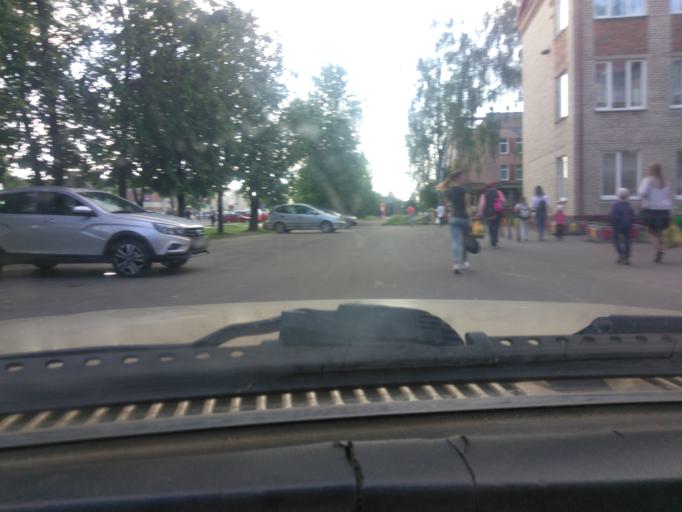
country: BY
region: Mogilev
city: Mahilyow
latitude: 53.9096
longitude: 30.3100
